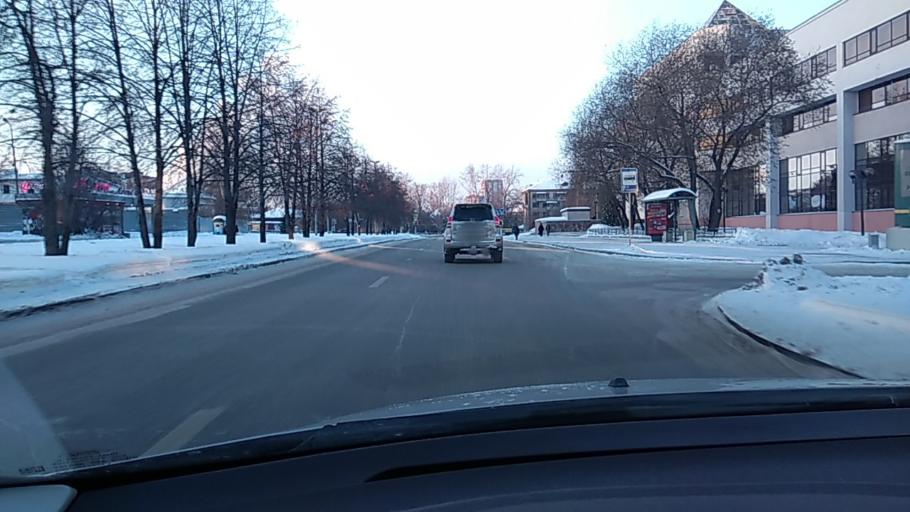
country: RU
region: Sverdlovsk
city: Yekaterinburg
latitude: 56.8449
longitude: 60.5891
